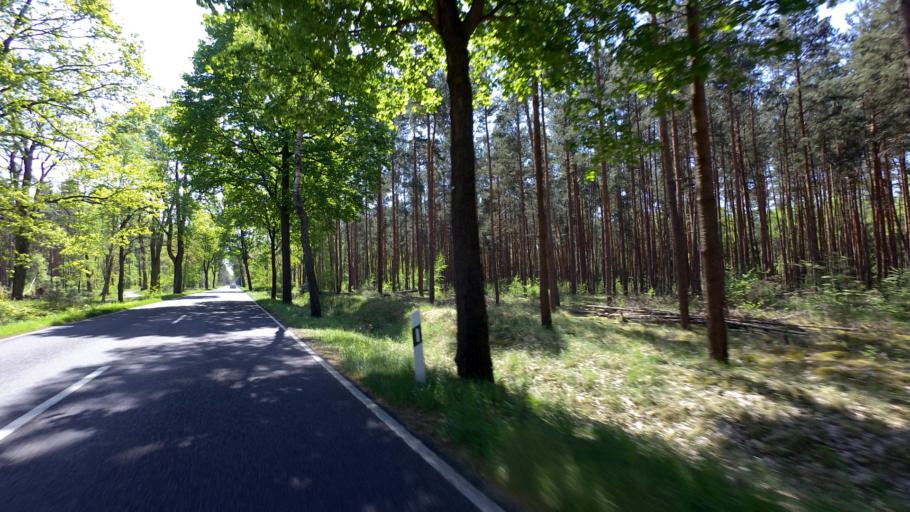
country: DE
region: Brandenburg
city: Halbe
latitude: 52.1478
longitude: 13.7463
